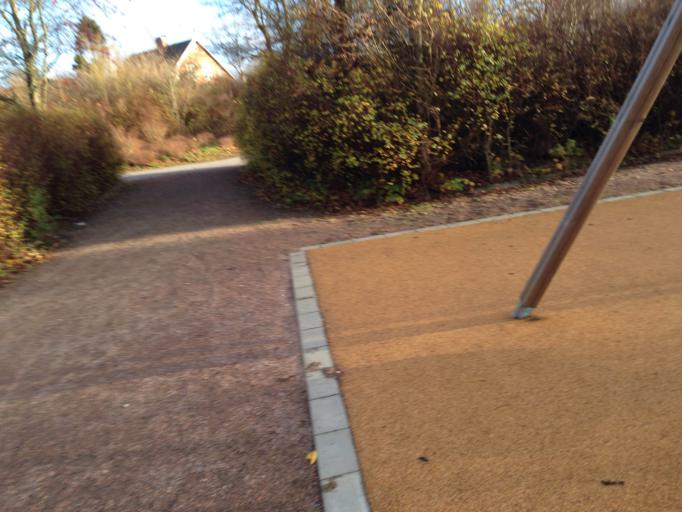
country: SE
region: Skane
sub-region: Lunds Kommun
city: Lund
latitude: 55.7186
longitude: 13.1787
